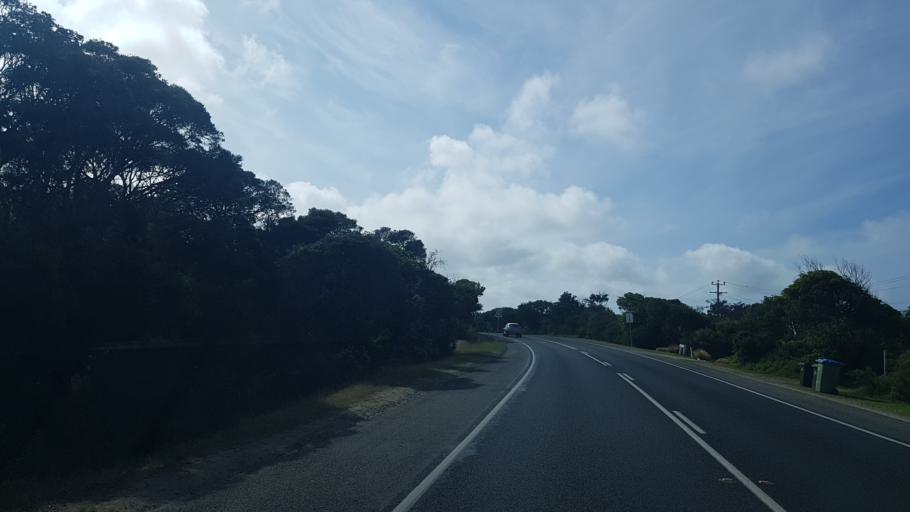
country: AU
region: Victoria
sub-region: Mornington Peninsula
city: Sorrento
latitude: -38.3551
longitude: 144.7527
